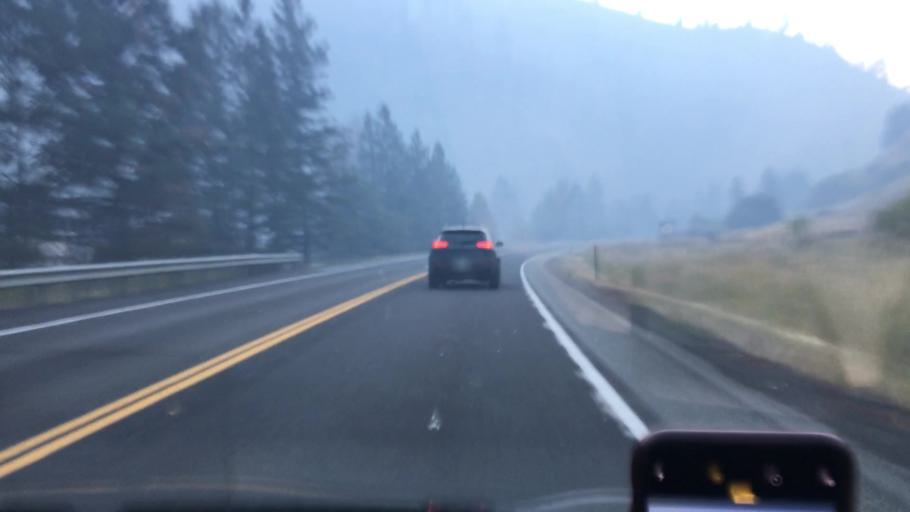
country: US
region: Idaho
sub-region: Valley County
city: McCall
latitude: 45.2699
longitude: -116.3450
